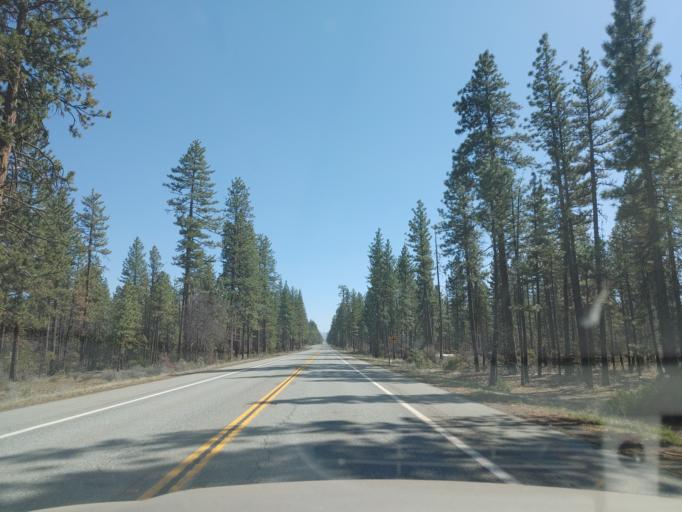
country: US
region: California
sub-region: Shasta County
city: Burney
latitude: 40.9933
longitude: -121.6282
